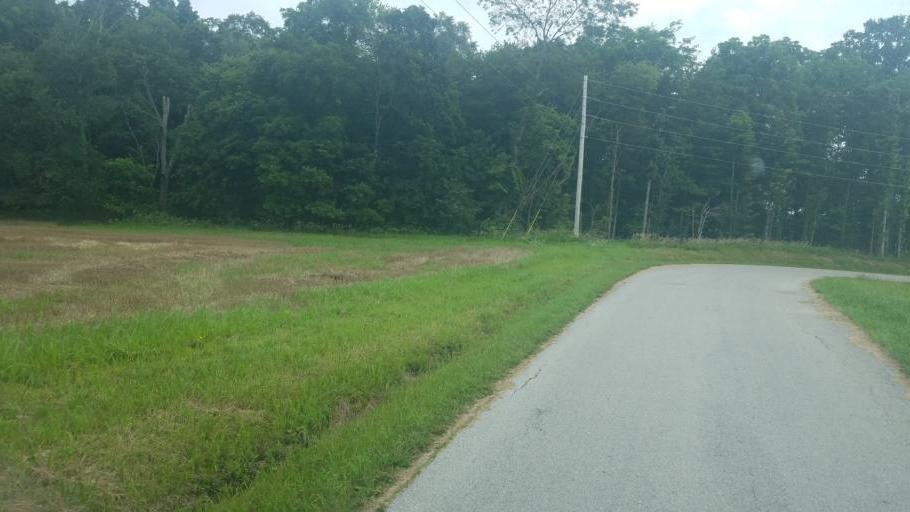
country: US
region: Ohio
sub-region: Morrow County
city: Cardington
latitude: 40.4943
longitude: -82.9505
